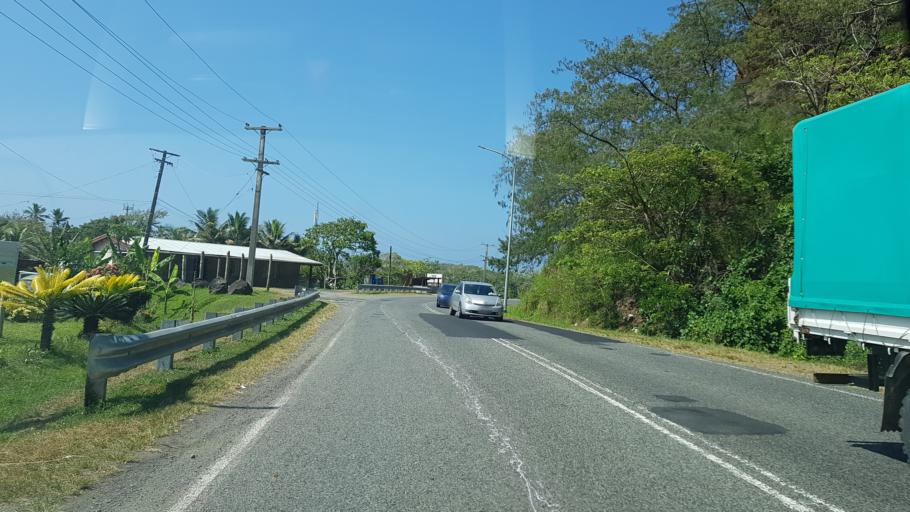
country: FJ
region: Western
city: Nadi
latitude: -18.1829
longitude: 177.6031
